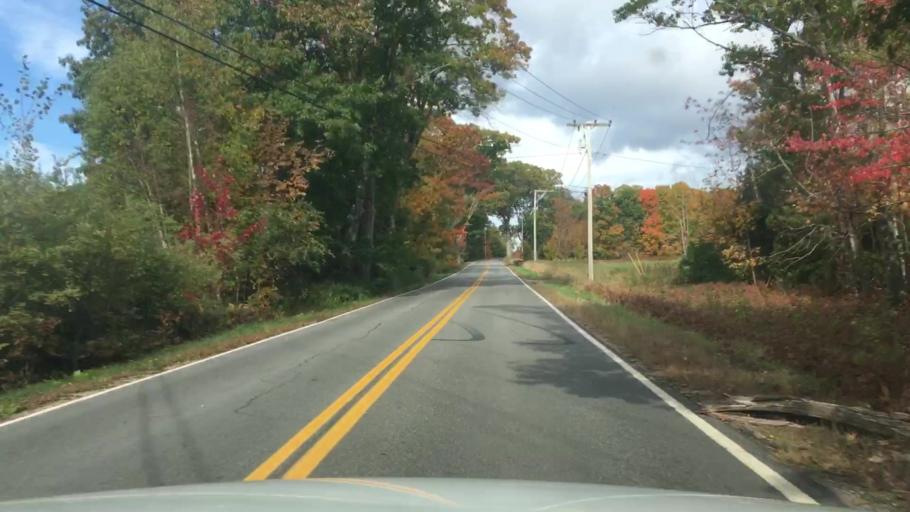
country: US
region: Maine
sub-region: Knox County
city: Hope
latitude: 44.3024
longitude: -69.1121
